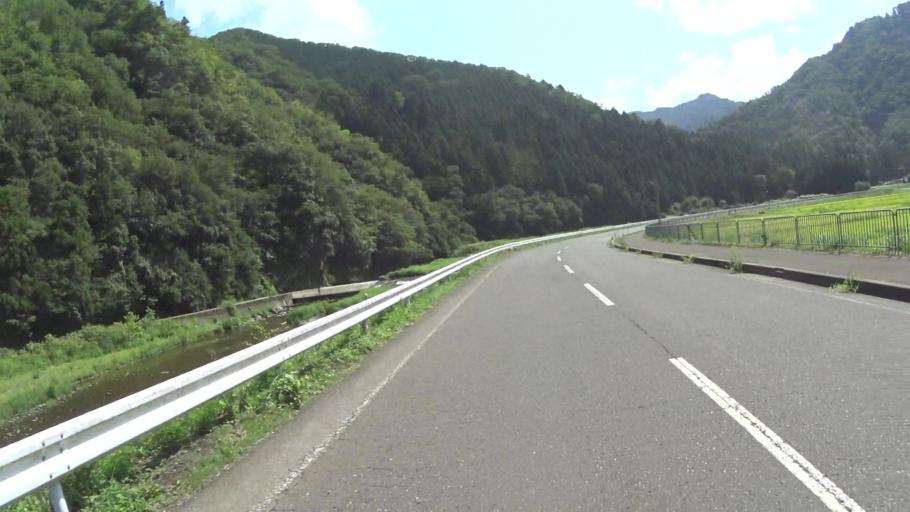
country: JP
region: Fukui
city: Obama
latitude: 35.4013
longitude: 135.6283
